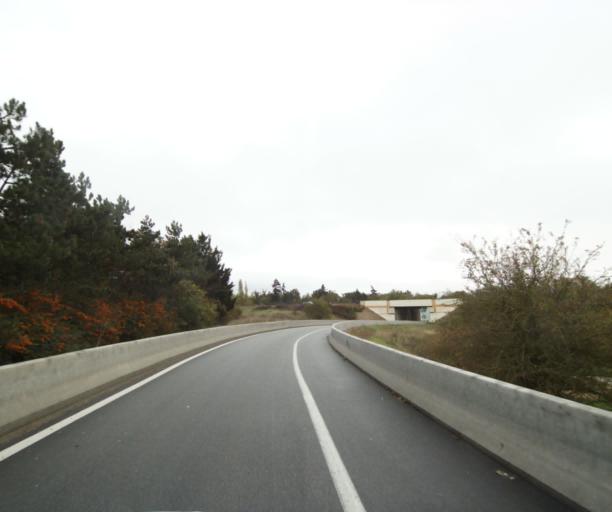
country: FR
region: Centre
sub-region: Departement d'Eure-et-Loir
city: Luray
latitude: 48.7464
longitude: 1.3926
